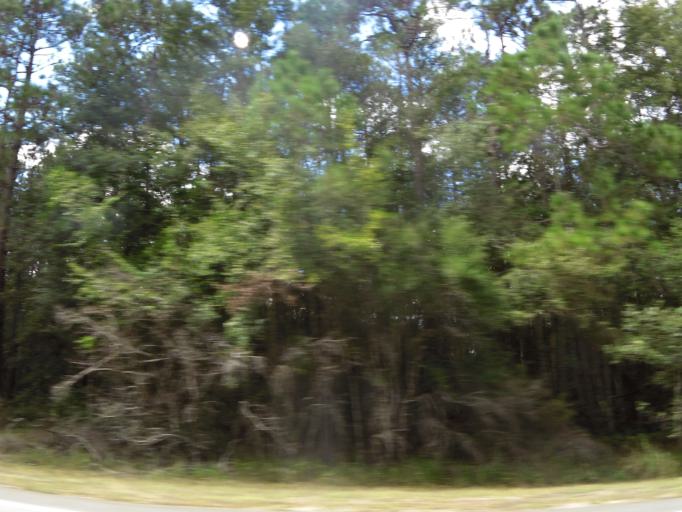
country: US
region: Georgia
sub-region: Charlton County
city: Folkston
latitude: 31.0131
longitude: -82.0258
